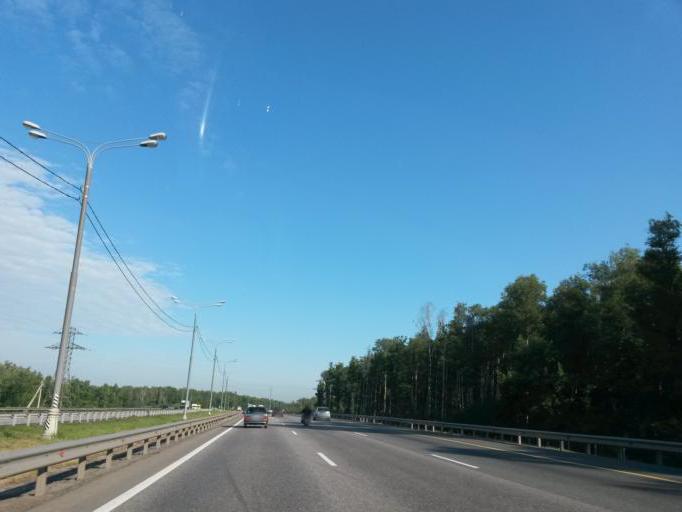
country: RU
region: Moskovskaya
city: Vostryakovo
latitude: 55.3615
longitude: 37.7931
